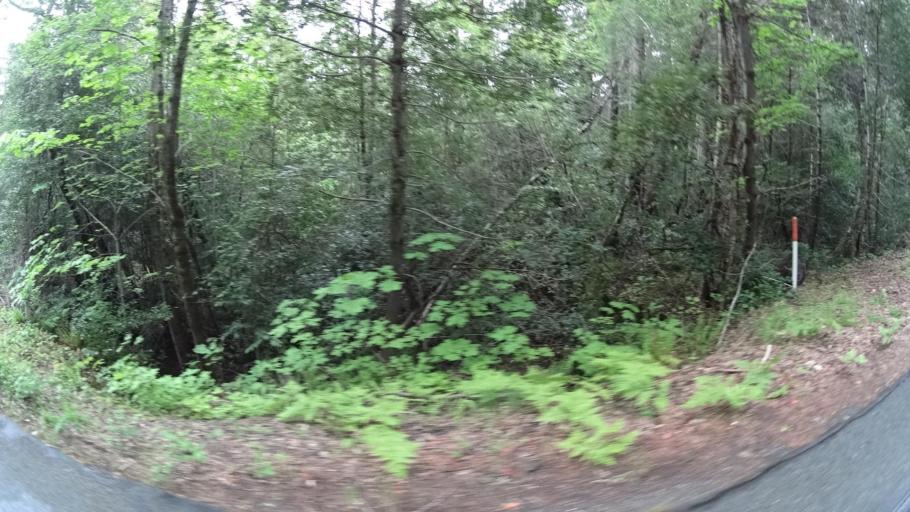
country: US
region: California
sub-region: Siskiyou County
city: Happy Camp
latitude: 41.3658
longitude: -123.5047
